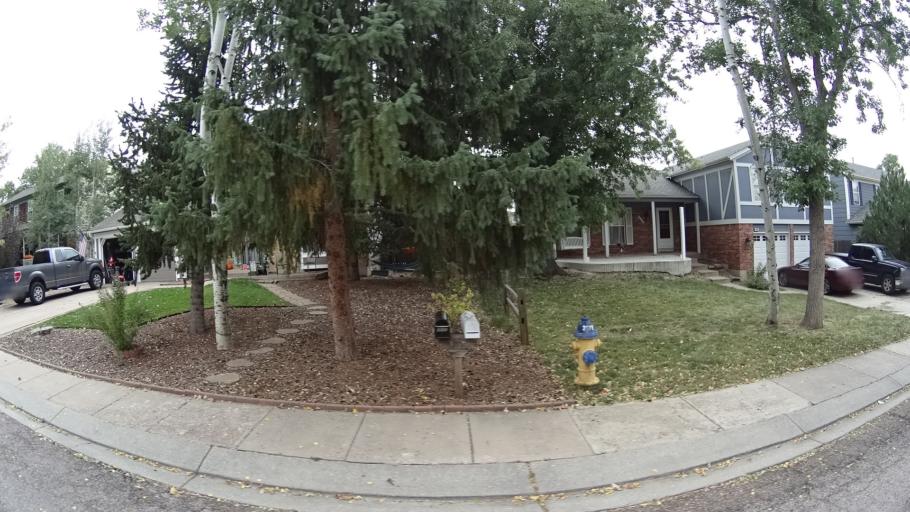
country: US
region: Colorado
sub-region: El Paso County
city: Cimarron Hills
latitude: 38.9019
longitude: -104.7318
